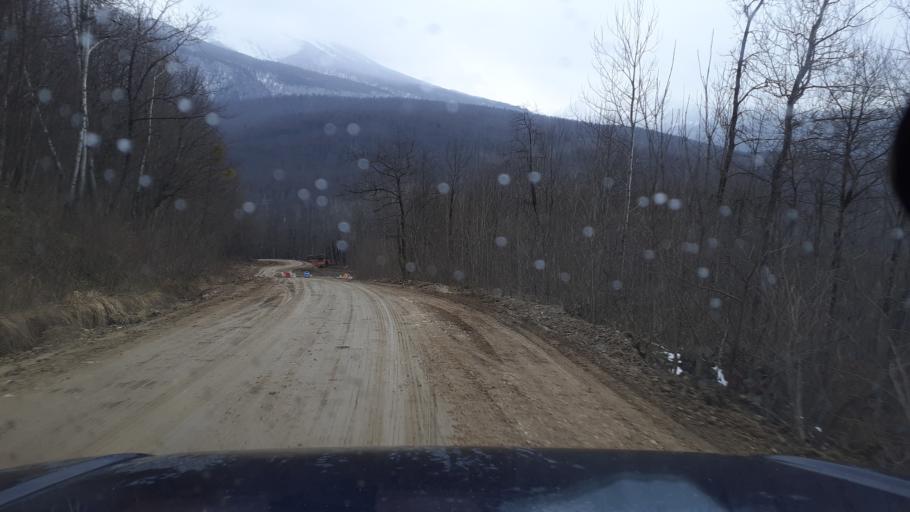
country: RU
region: Krasnodarskiy
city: Neftegorsk
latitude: 44.1651
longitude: 39.8148
